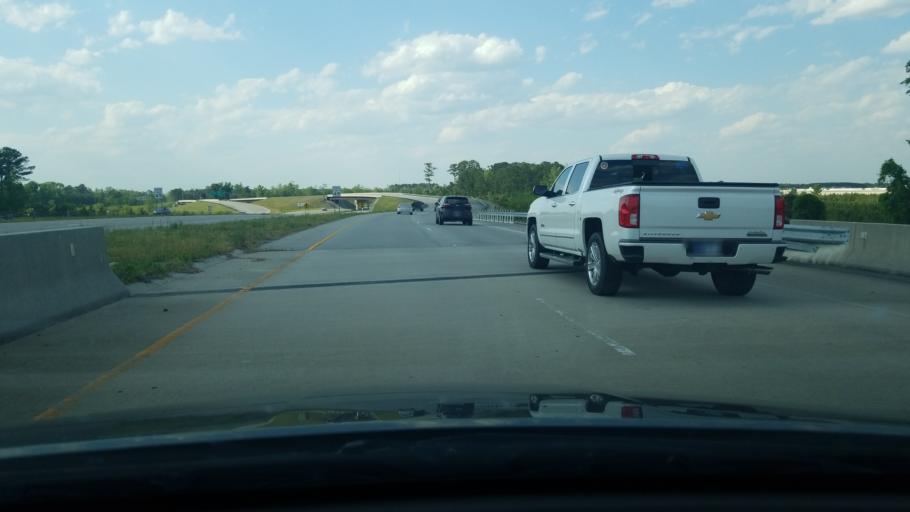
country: US
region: North Carolina
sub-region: Onslow County
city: Pumpkin Center
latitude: 34.7688
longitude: -77.3961
